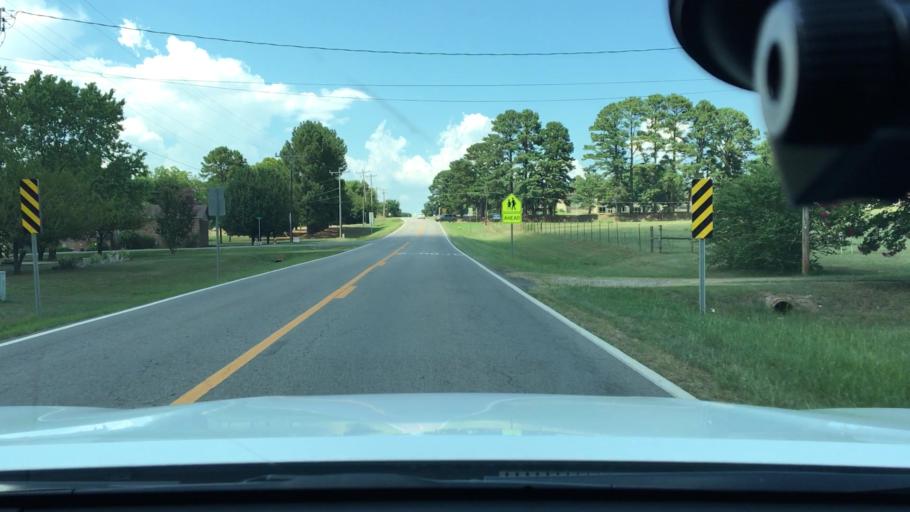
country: US
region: Arkansas
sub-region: Logan County
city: Paris
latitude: 35.2956
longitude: -93.6366
